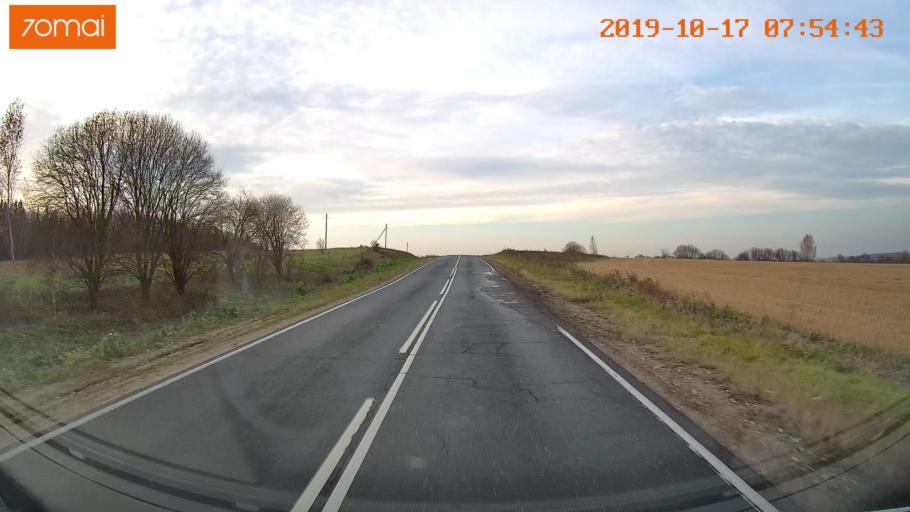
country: RU
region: Vladimir
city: Bavleny
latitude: 56.4456
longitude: 39.6045
